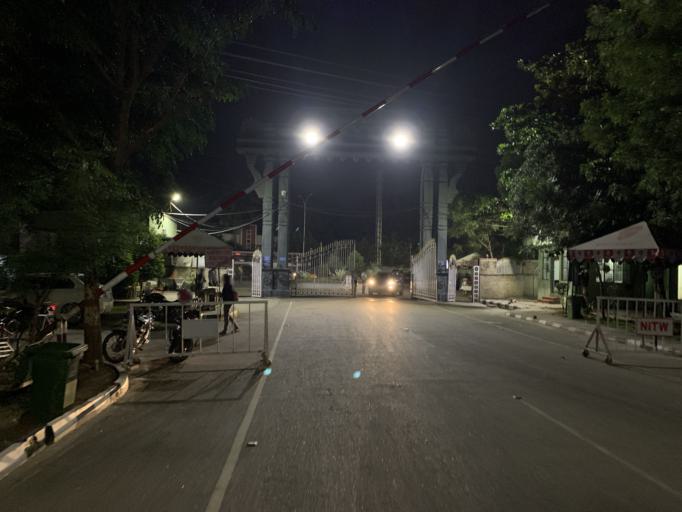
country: IN
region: Telangana
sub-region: Warangal
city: Warangal
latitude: 17.9880
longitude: 79.5307
